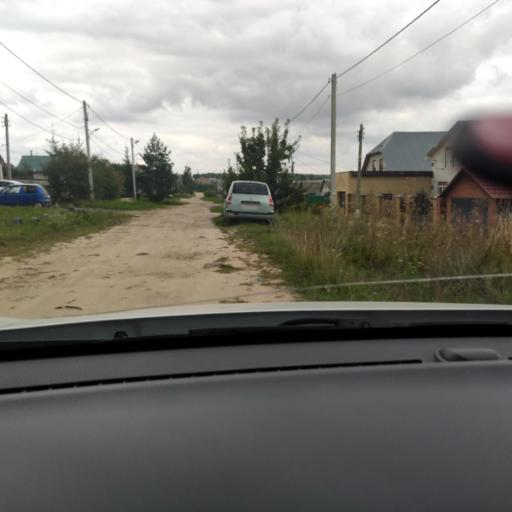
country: RU
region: Tatarstan
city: Vysokaya Gora
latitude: 55.8181
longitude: 49.2599
